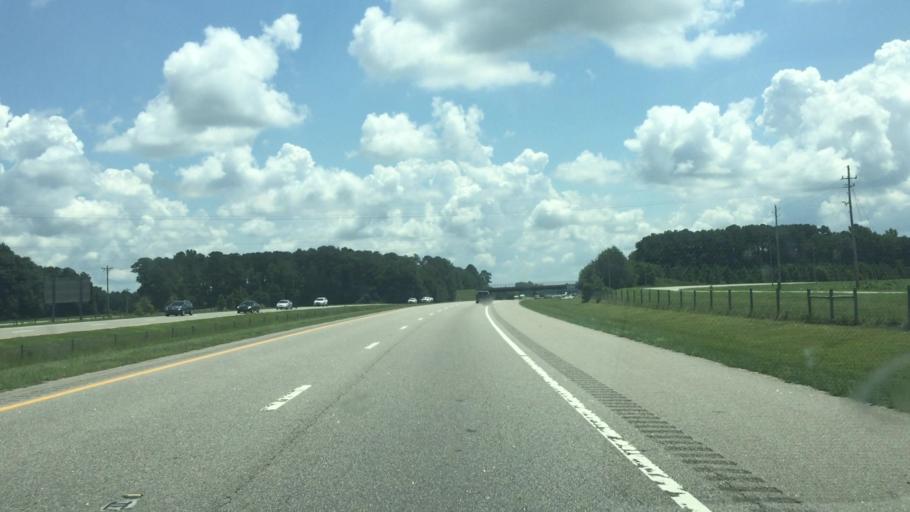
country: US
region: North Carolina
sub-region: Robeson County
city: Lumberton
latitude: 34.5922
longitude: -79.0741
